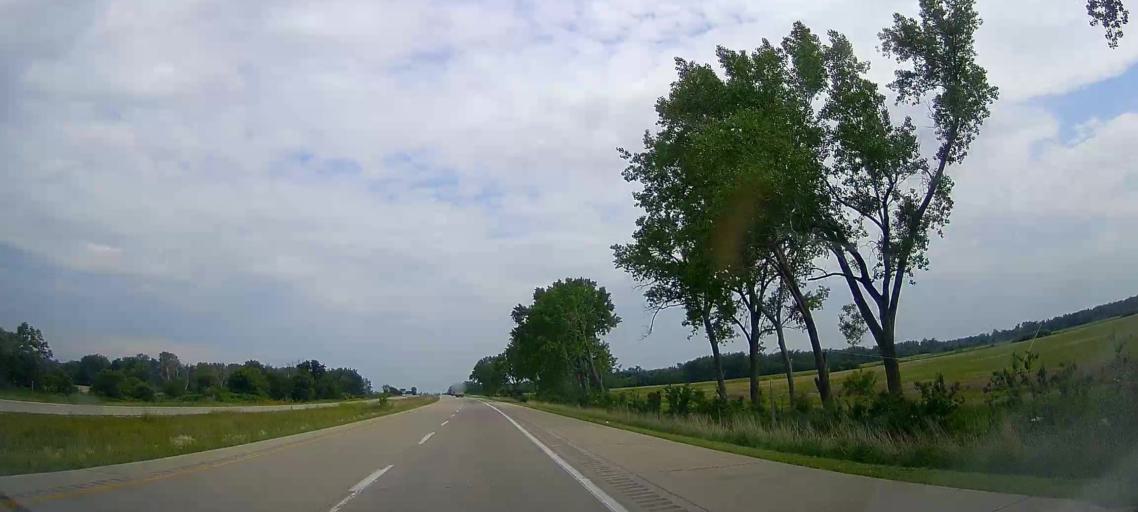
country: US
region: Nebraska
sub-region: Burt County
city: Tekamah
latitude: 41.8243
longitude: -96.0758
